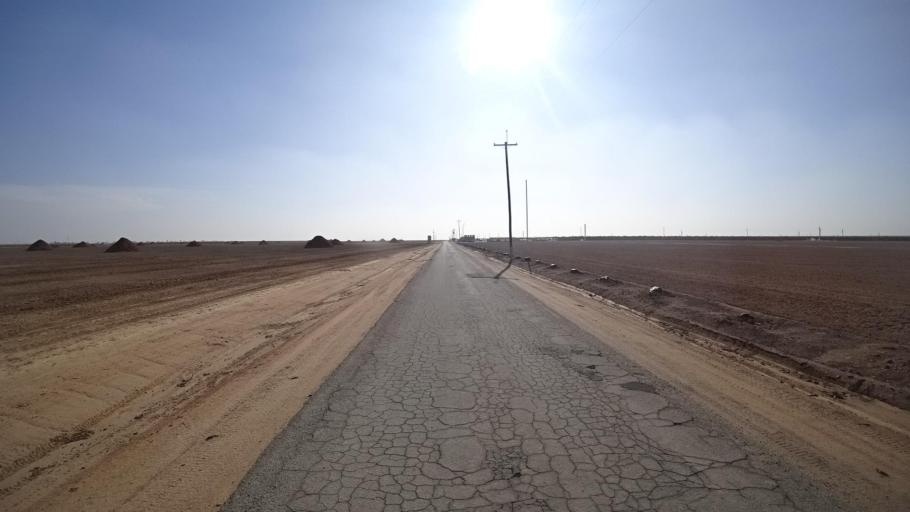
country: US
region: California
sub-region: Kern County
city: Shafter
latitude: 35.5396
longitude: -119.1336
